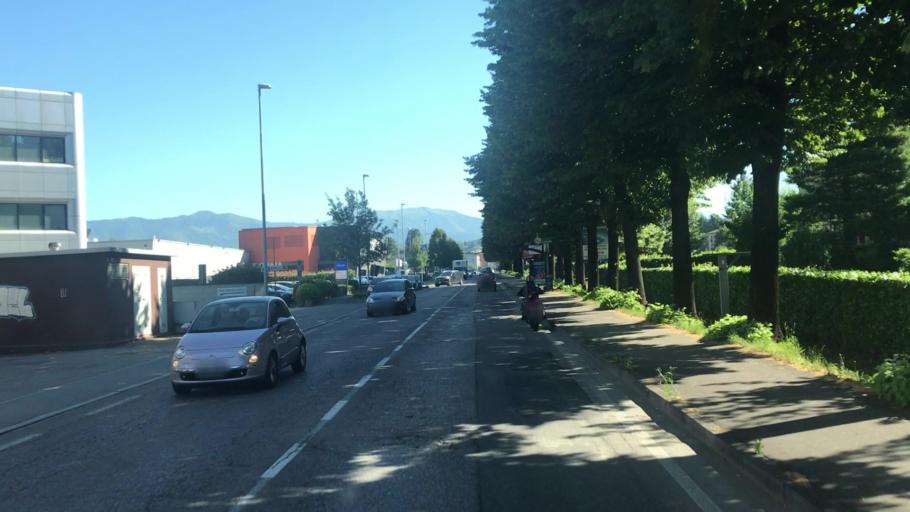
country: IT
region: Lombardy
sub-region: Provincia di Como
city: Cantu
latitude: 45.7416
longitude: 9.1195
